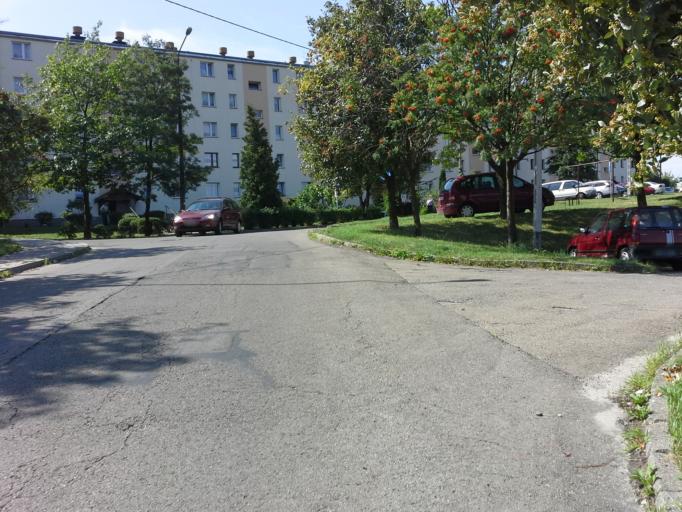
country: PL
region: Lesser Poland Voivodeship
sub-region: Powiat chrzanowski
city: Trzebinia
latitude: 50.1617
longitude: 19.4775
